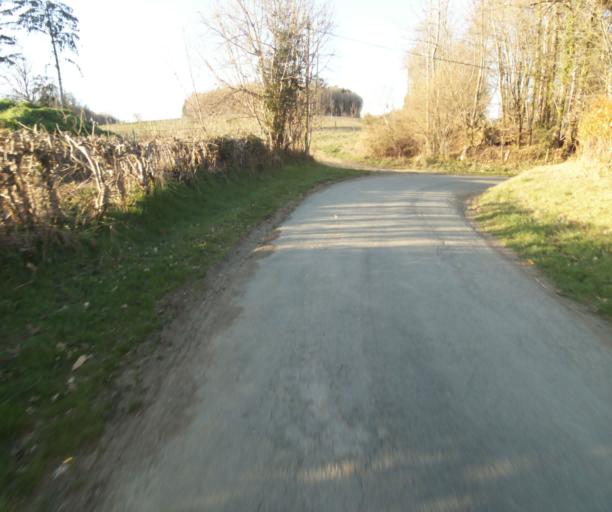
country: FR
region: Limousin
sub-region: Departement de la Correze
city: Uzerche
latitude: 45.3734
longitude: 1.6044
